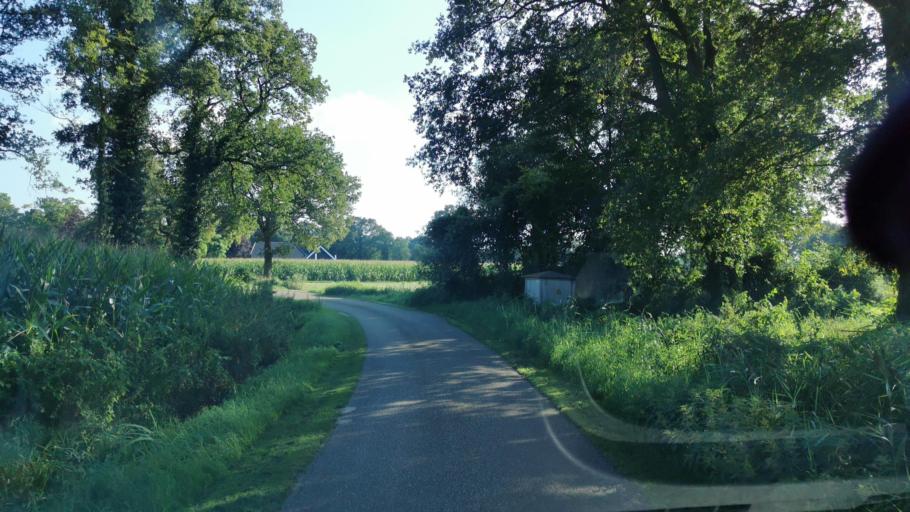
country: NL
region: Overijssel
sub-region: Gemeente Tubbergen
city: Tubbergen
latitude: 52.3558
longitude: 6.8144
